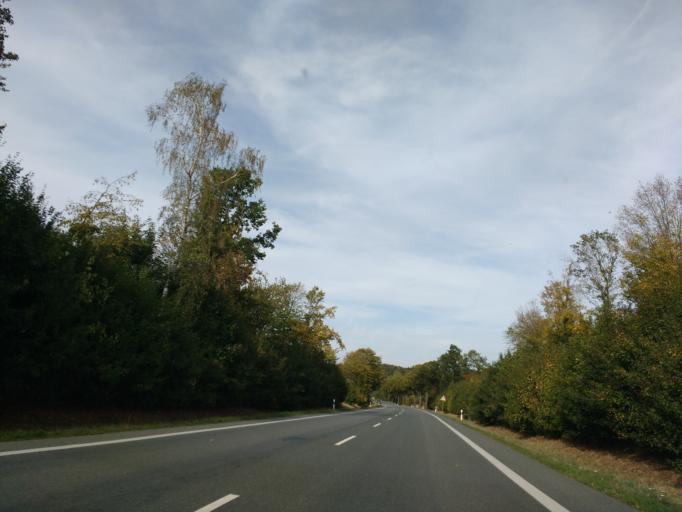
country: DE
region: North Rhine-Westphalia
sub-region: Regierungsbezirk Detmold
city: Willebadessen
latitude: 51.6184
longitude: 9.1367
